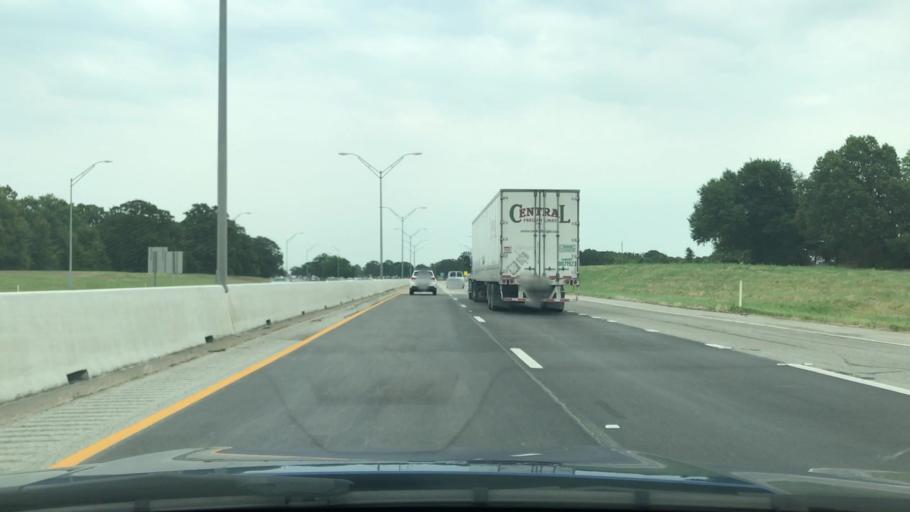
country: US
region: Texas
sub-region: Van Zandt County
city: Van
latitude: 32.5170
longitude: -95.6932
